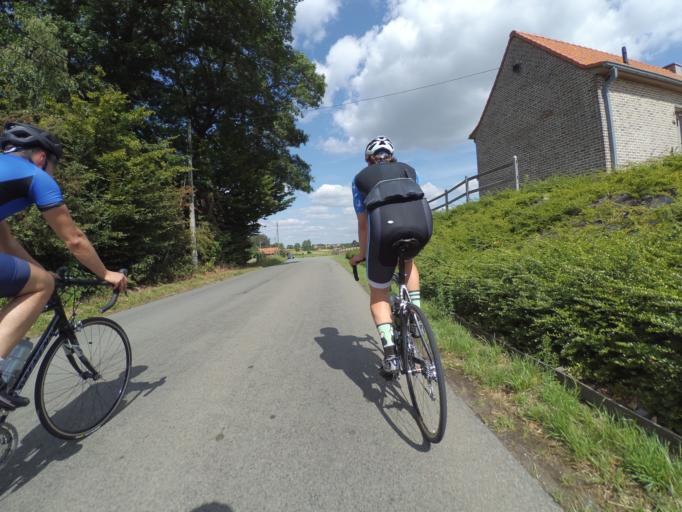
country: BE
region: Wallonia
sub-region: Province du Hainaut
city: Ellezelles
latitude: 50.7648
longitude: 3.6792
